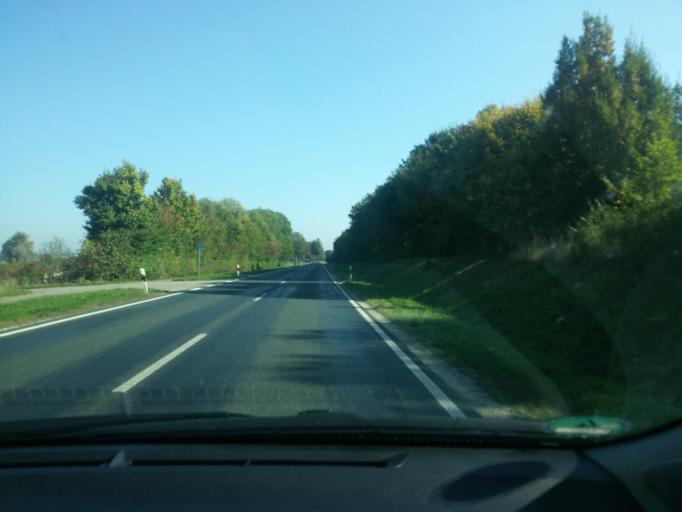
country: DE
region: Bavaria
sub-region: Swabia
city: Hainsfarth
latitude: 48.9734
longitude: 10.6207
